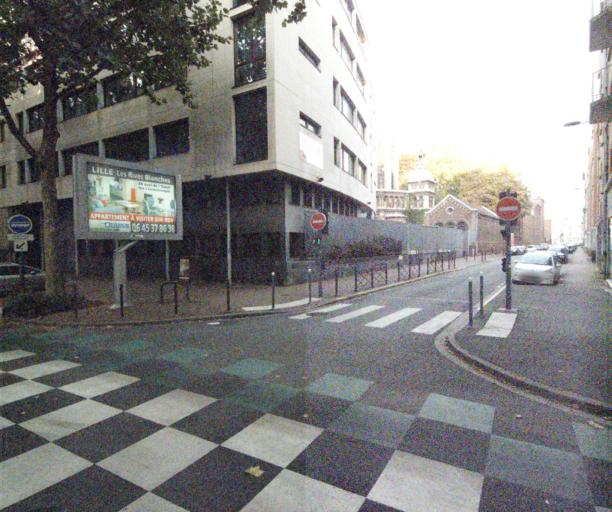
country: FR
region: Nord-Pas-de-Calais
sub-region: Departement du Nord
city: Lille
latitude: 50.6337
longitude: 3.0480
